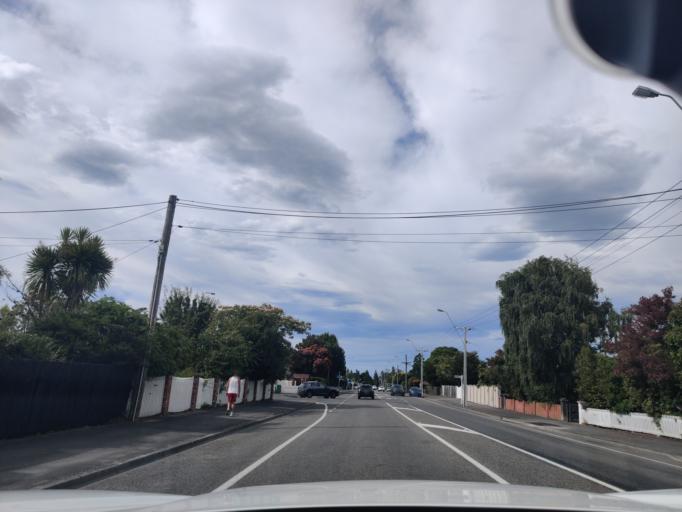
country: NZ
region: Wellington
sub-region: Masterton District
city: Masterton
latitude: -40.9411
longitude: 175.6701
